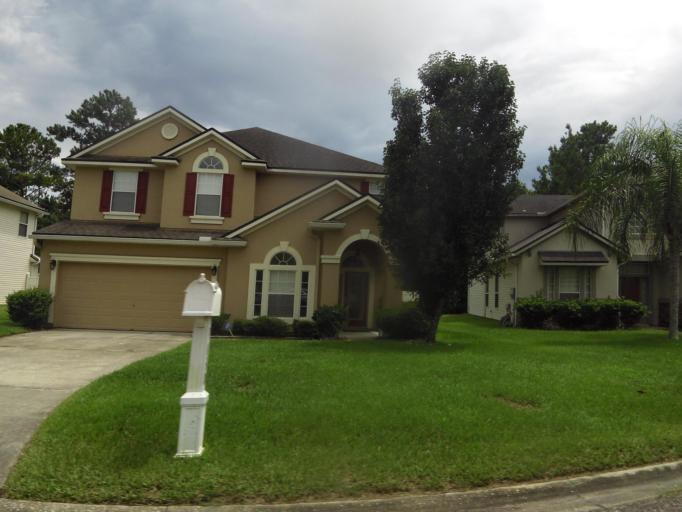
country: US
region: Florida
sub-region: Duval County
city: Jacksonville
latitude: 30.4263
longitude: -81.7181
